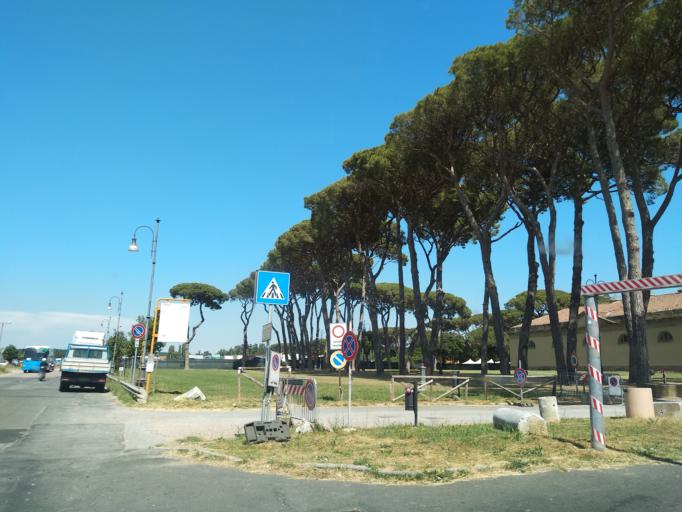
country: IT
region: Tuscany
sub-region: Provincia di Livorno
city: Livorno
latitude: 43.5689
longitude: 10.3633
